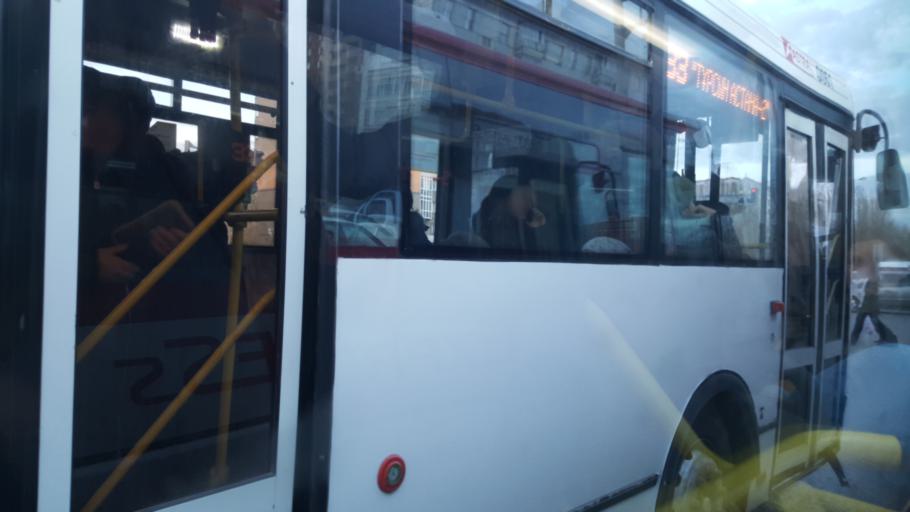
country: KZ
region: Astana Qalasy
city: Astana
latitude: 51.1545
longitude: 71.4859
